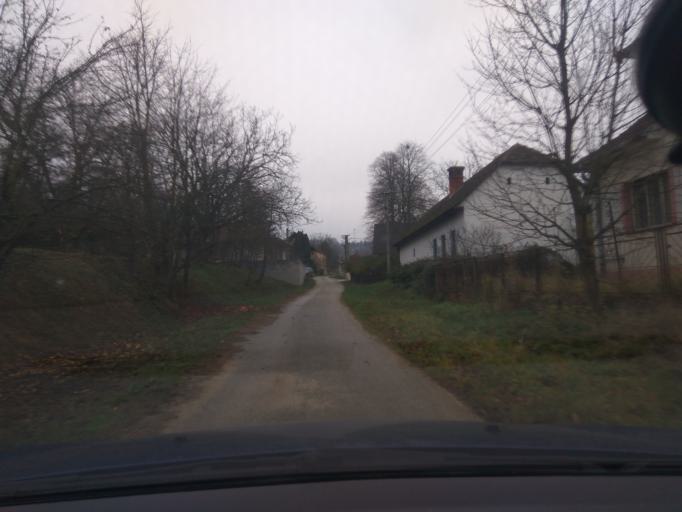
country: SK
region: Trnavsky
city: Vrbove
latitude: 48.6735
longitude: 17.6810
